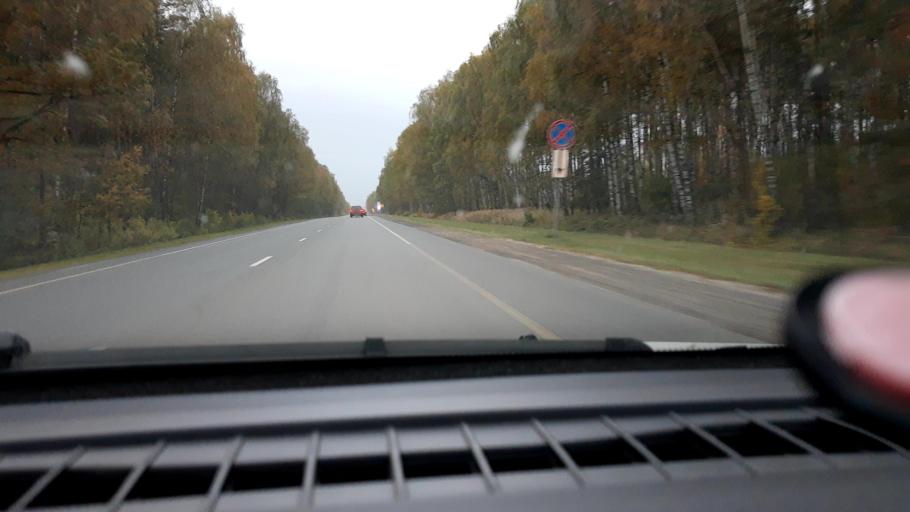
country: RU
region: Vladimir
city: Orgtrud
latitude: 56.2100
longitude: 40.6200
